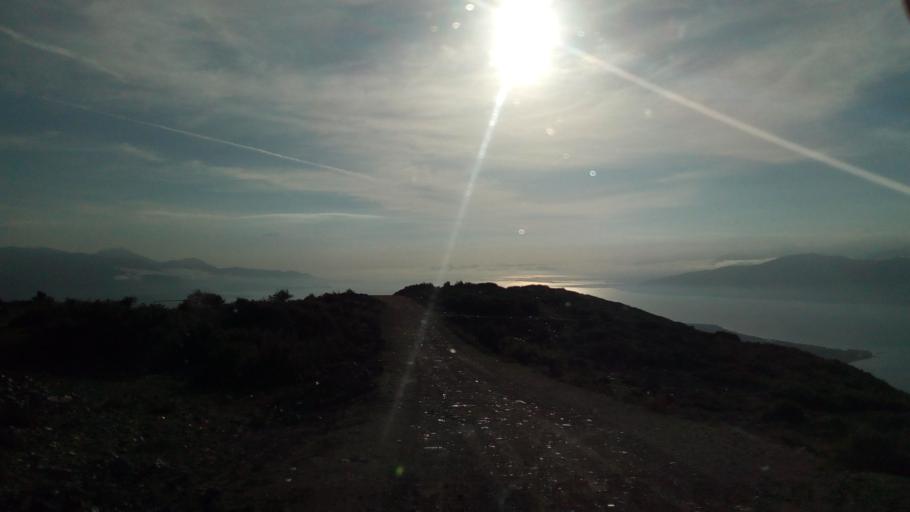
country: GR
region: West Greece
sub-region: Nomos Aitolias kai Akarnanias
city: Nafpaktos
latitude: 38.4153
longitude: 21.8146
